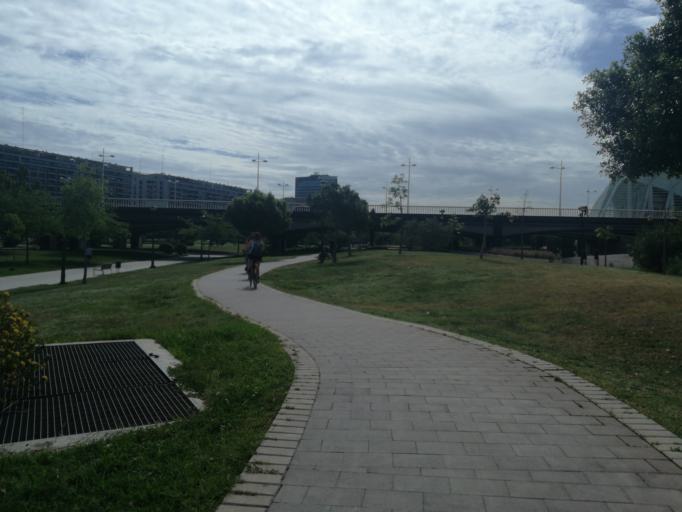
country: ES
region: Valencia
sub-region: Provincia de Valencia
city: Valencia
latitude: 39.4588
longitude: -0.3552
